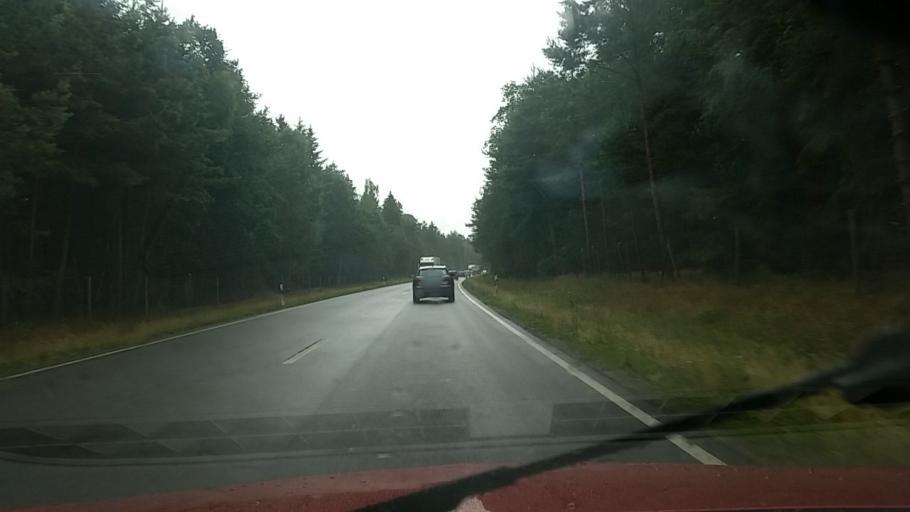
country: DE
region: Lower Saxony
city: Wagenhoff
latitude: 52.5395
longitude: 10.5067
